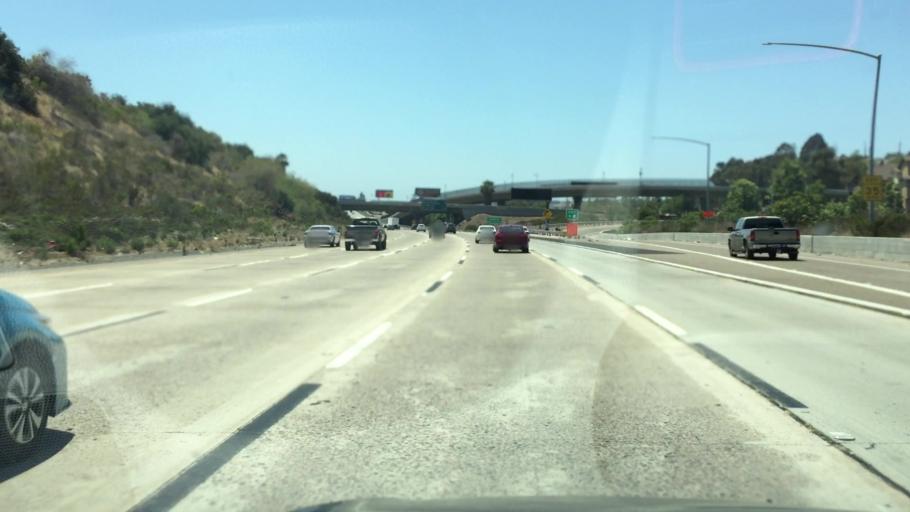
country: US
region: California
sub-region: San Diego County
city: La Mesa
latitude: 32.7811
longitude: -117.0848
